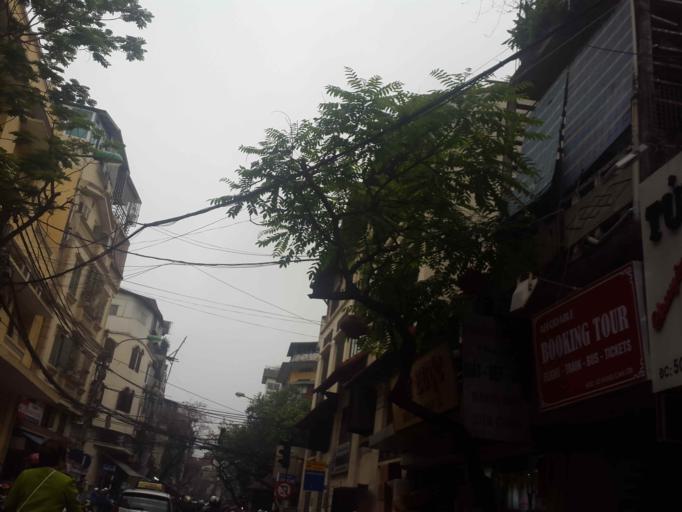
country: VN
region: Ha Noi
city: Hoan Kiem
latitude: 21.0344
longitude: 105.8497
